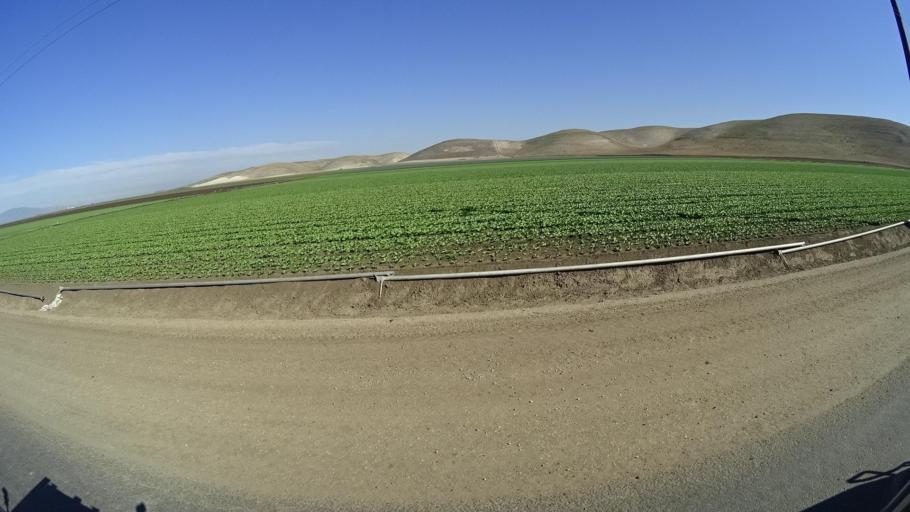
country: US
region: California
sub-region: Monterey County
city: King City
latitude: 36.1763
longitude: -121.0389
